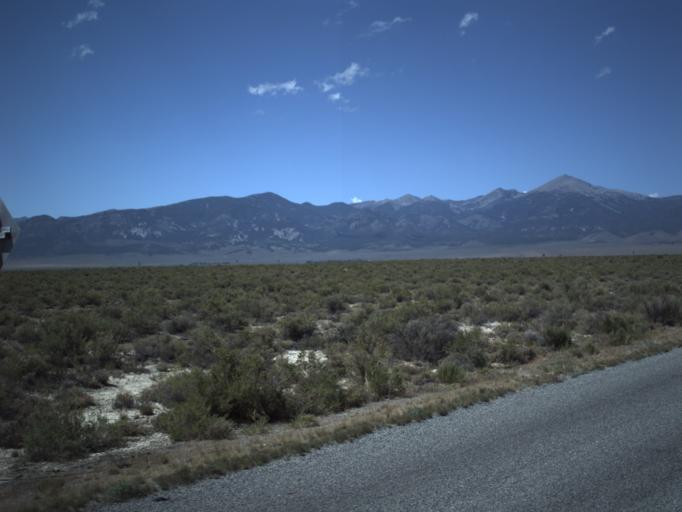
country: US
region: Nevada
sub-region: White Pine County
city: McGill
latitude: 39.0559
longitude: -114.0326
